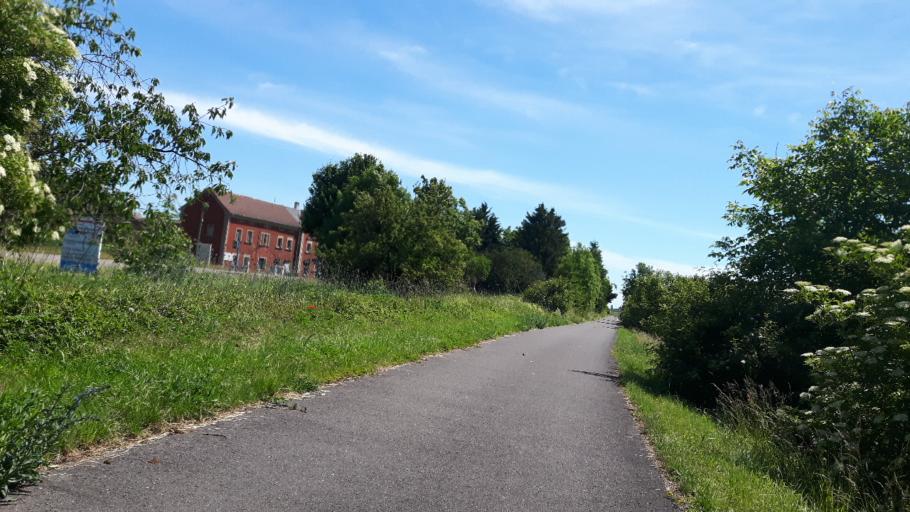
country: DE
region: Saxony-Anhalt
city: Lutzen
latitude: 51.2397
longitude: 12.1125
